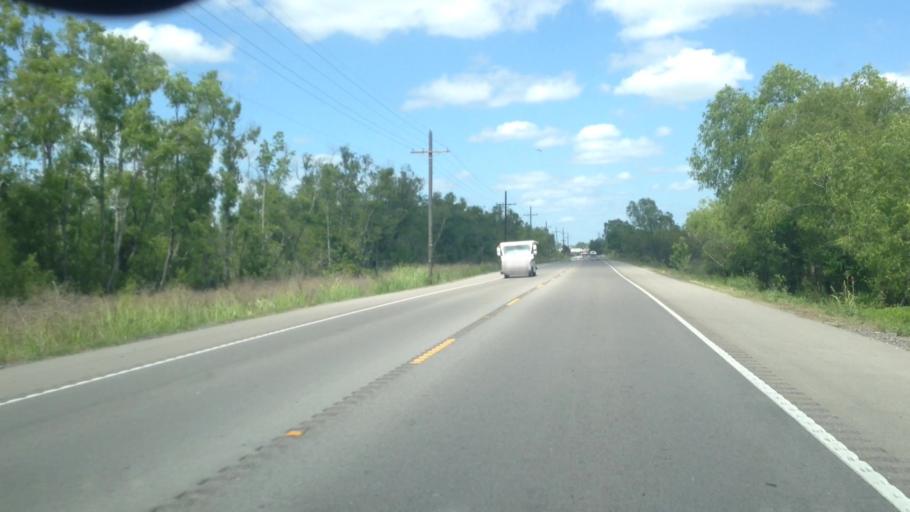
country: US
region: Louisiana
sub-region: Terrebonne Parish
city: Houma
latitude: 29.6370
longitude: -90.6975
